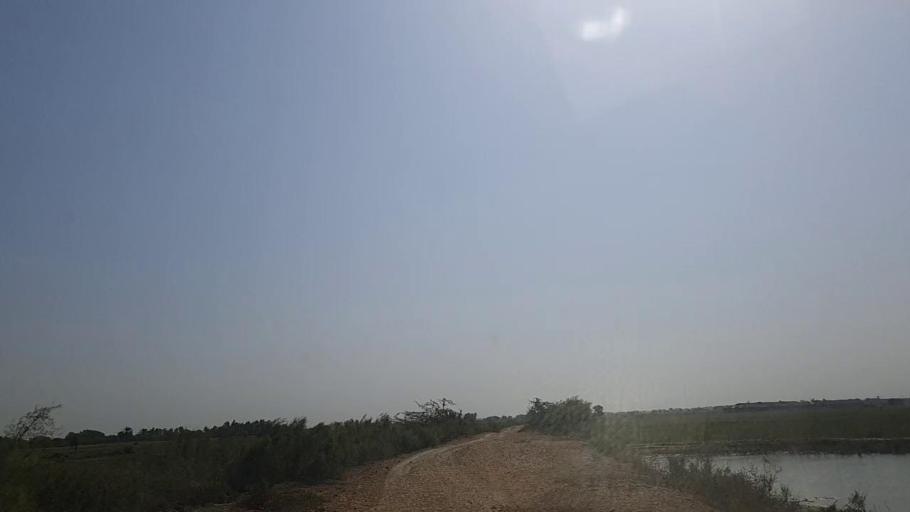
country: PK
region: Sindh
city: Daro Mehar
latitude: 24.7134
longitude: 68.1207
